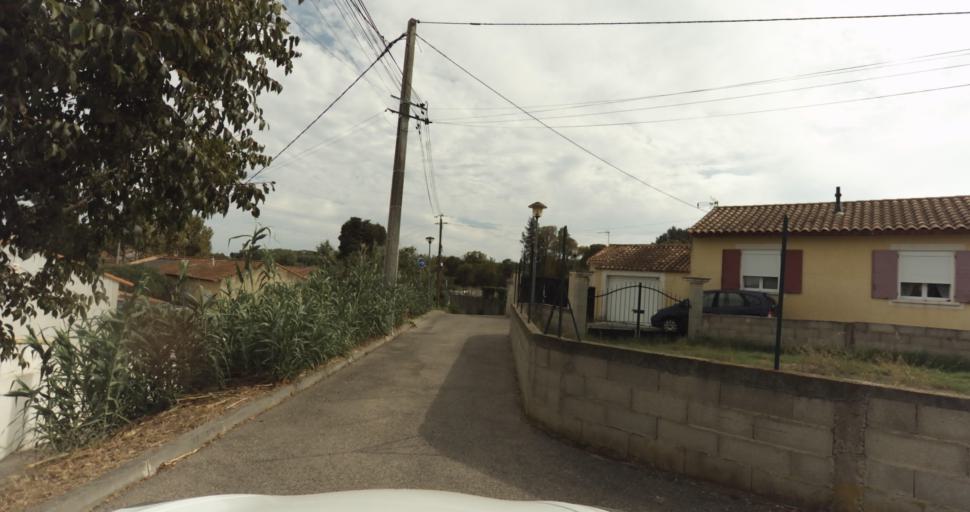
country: FR
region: Provence-Alpes-Cote d'Azur
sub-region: Departement des Bouches-du-Rhone
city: Miramas
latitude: 43.5725
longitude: 5.0136
